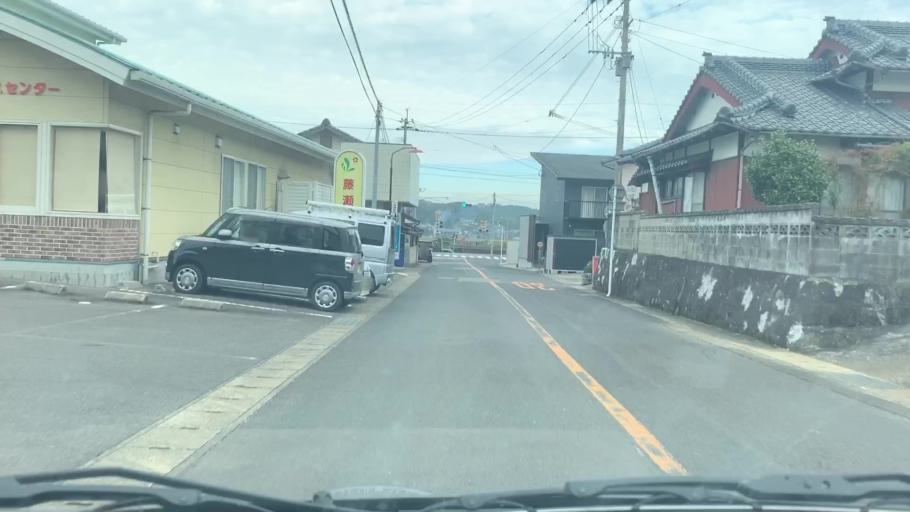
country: JP
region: Saga Prefecture
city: Takeocho-takeo
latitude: 33.1955
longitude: 129.9629
